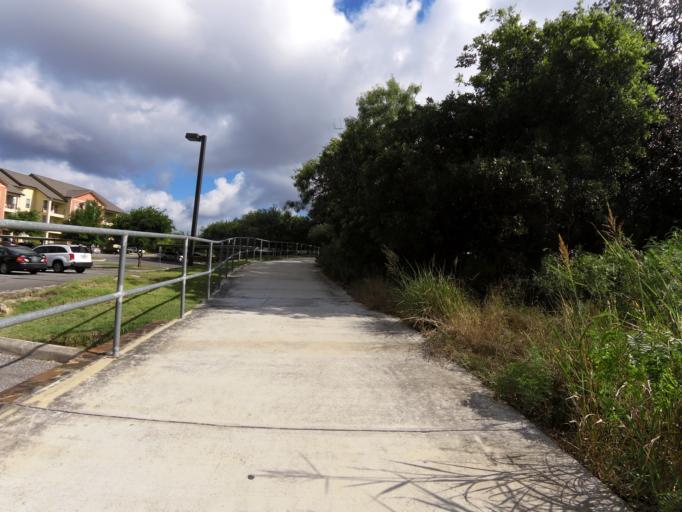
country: US
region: Texas
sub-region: Bexar County
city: Shavano Park
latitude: 29.5774
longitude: -98.6081
